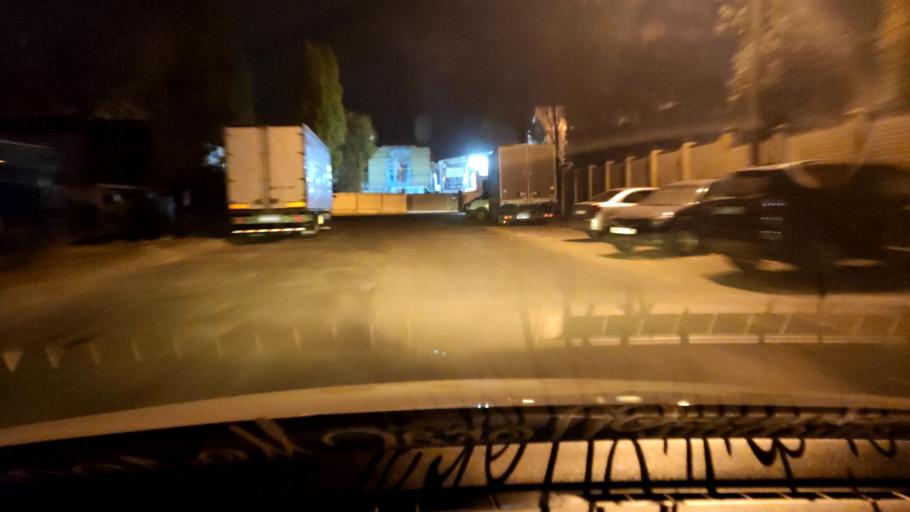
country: RU
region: Voronezj
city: Voronezh
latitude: 51.6625
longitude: 39.1592
